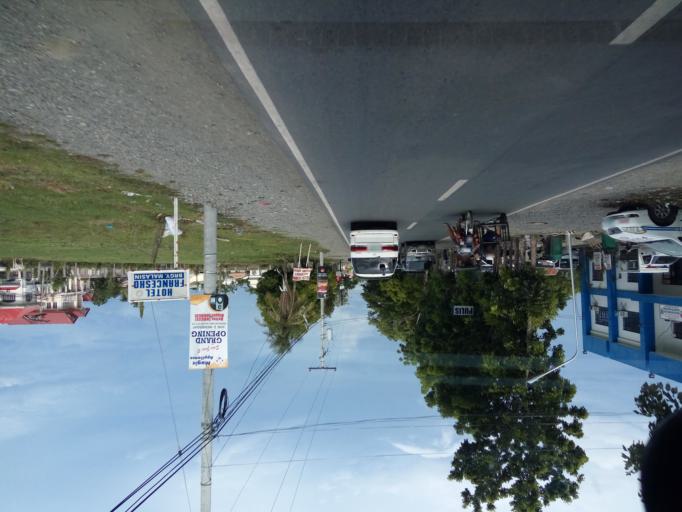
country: PH
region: Central Luzon
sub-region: Province of Nueva Ecija
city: Sibul
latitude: 15.7964
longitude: 120.9779
